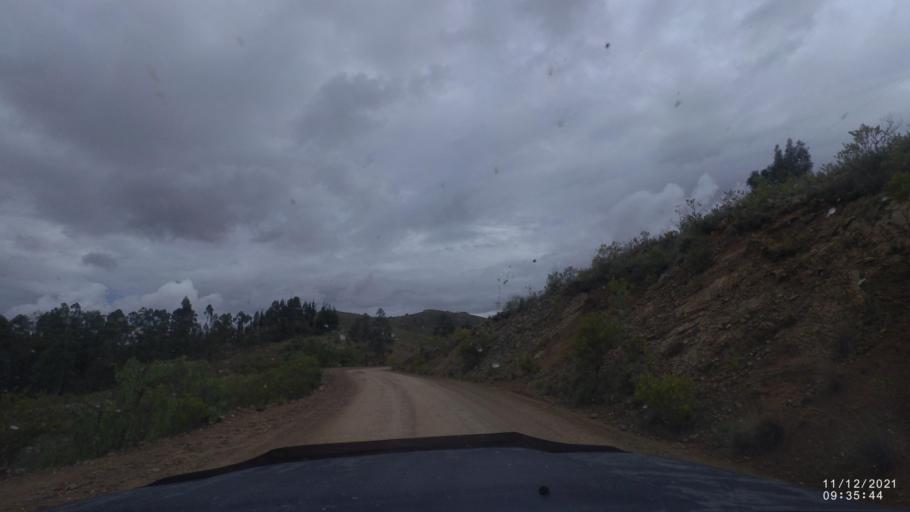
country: BO
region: Cochabamba
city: Tarata
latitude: -17.8265
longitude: -65.9905
